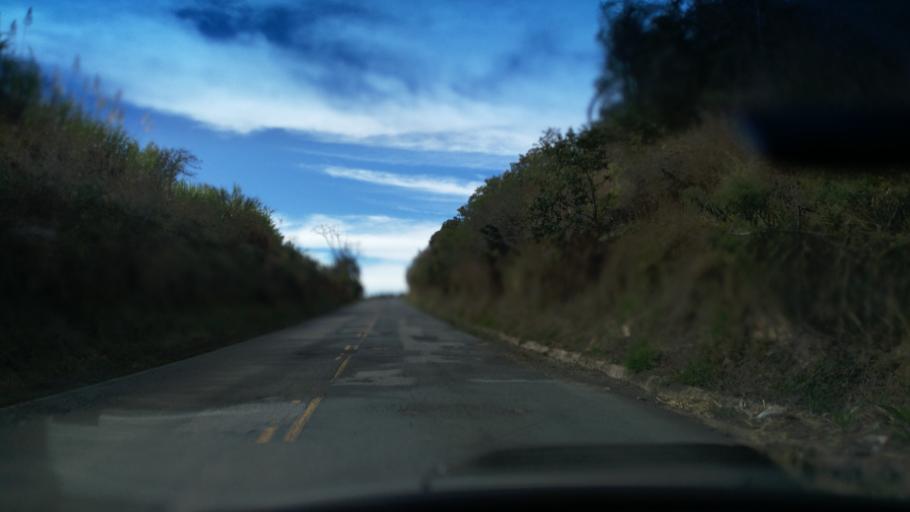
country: BR
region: Minas Gerais
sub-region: Andradas
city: Andradas
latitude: -22.0617
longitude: -46.3890
